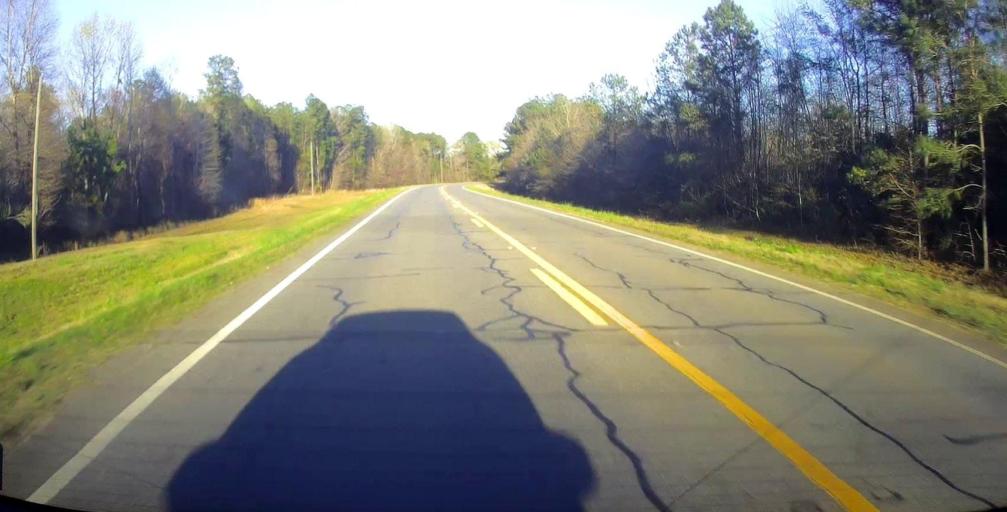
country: US
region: Georgia
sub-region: Wilcox County
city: Abbeville
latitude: 32.0012
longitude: -83.2519
